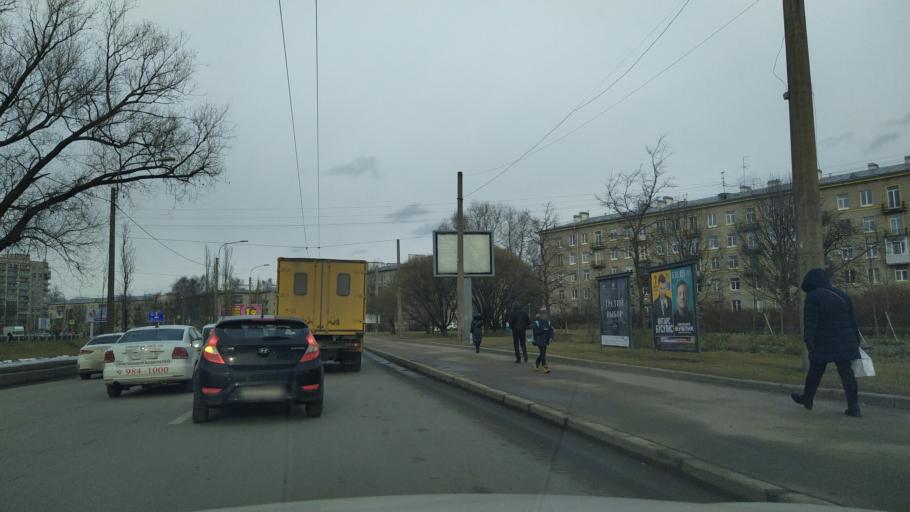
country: RU
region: Leningrad
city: Chernaya Rechka
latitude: 59.9877
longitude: 30.3024
